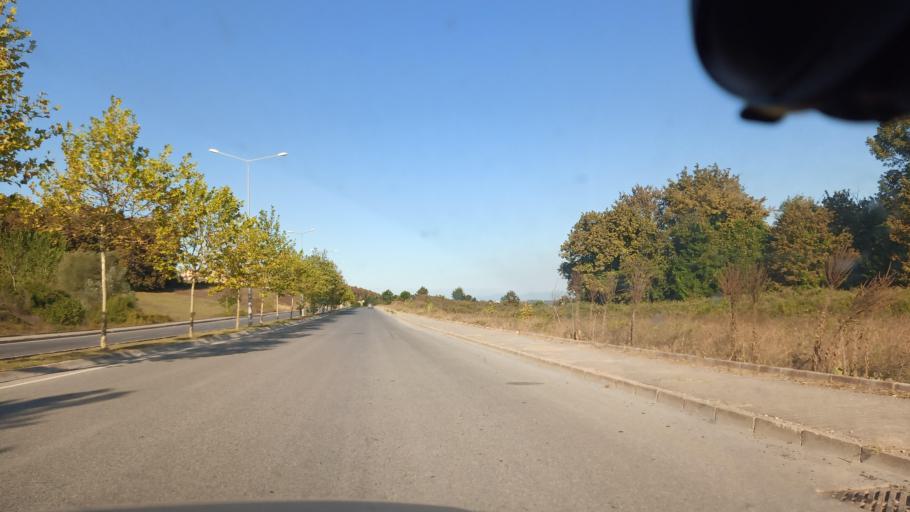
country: TR
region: Sakarya
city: Kazimpasa
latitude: 40.8507
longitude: 30.2824
